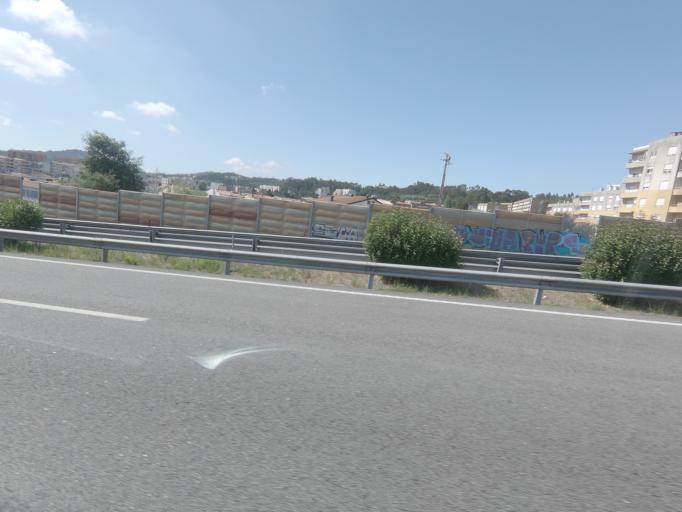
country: PT
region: Porto
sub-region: Valongo
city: Valongo
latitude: 41.1987
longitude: -8.5129
